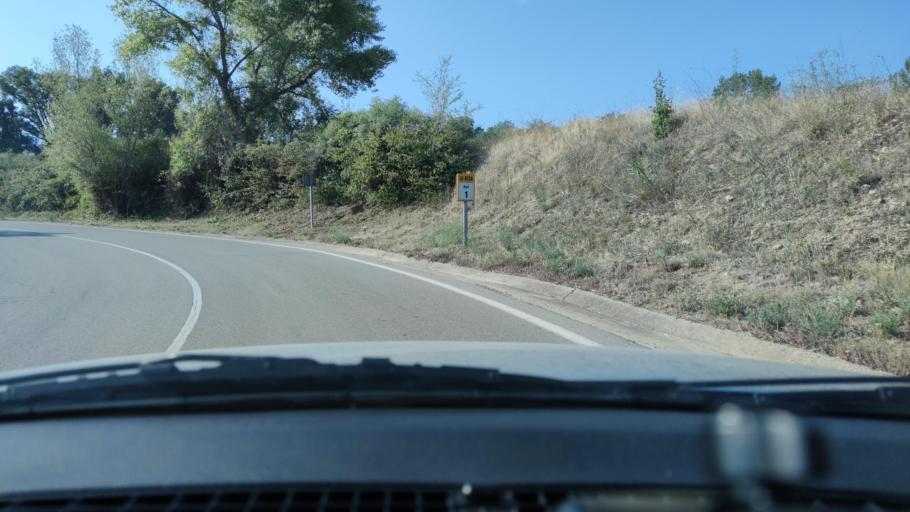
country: ES
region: Catalonia
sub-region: Provincia de Lleida
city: Llimiana
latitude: 42.0972
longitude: 0.8831
